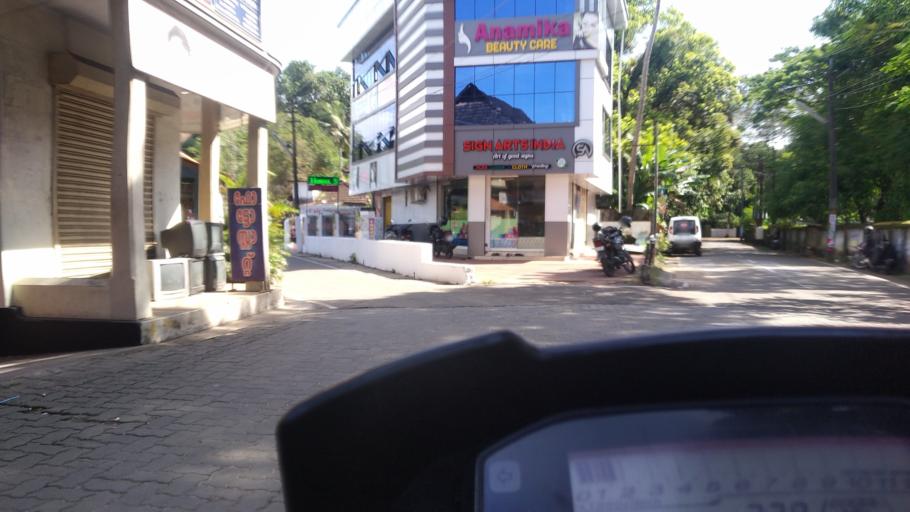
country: IN
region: Kerala
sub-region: Thrissur District
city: Kodungallur
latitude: 10.1485
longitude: 76.2321
